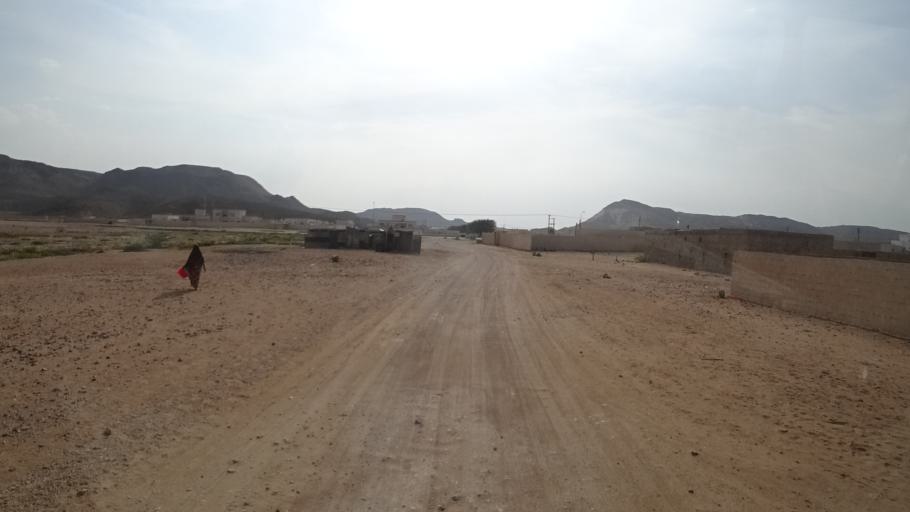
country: OM
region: Ash Sharqiyah
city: Sur
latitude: 22.4326
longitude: 59.8268
